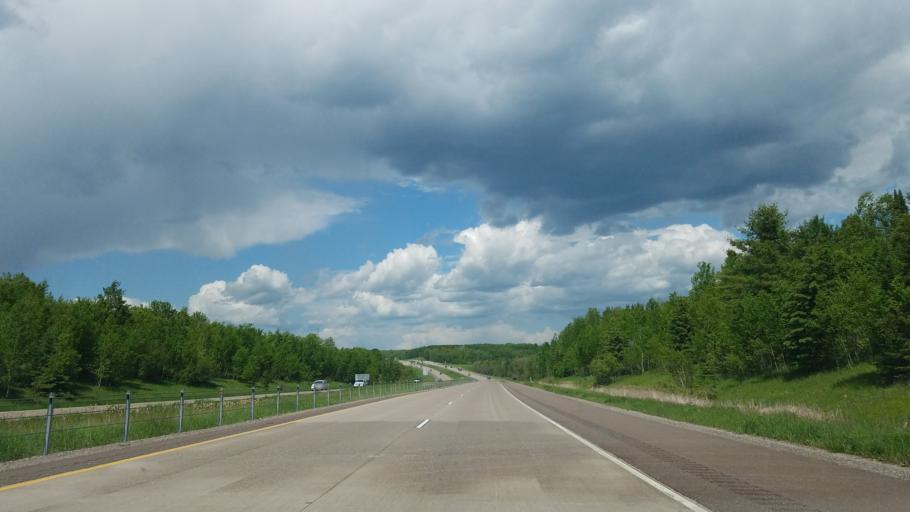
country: US
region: Minnesota
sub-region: Carlton County
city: Moose Lake
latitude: 46.4456
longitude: -92.7379
